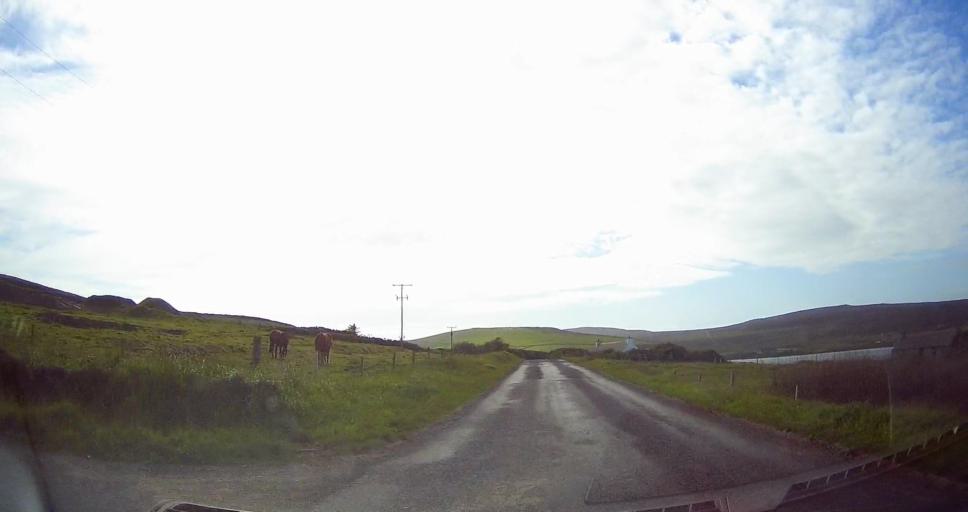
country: GB
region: Scotland
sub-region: Orkney Islands
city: Stromness
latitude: 58.7849
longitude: -3.2448
